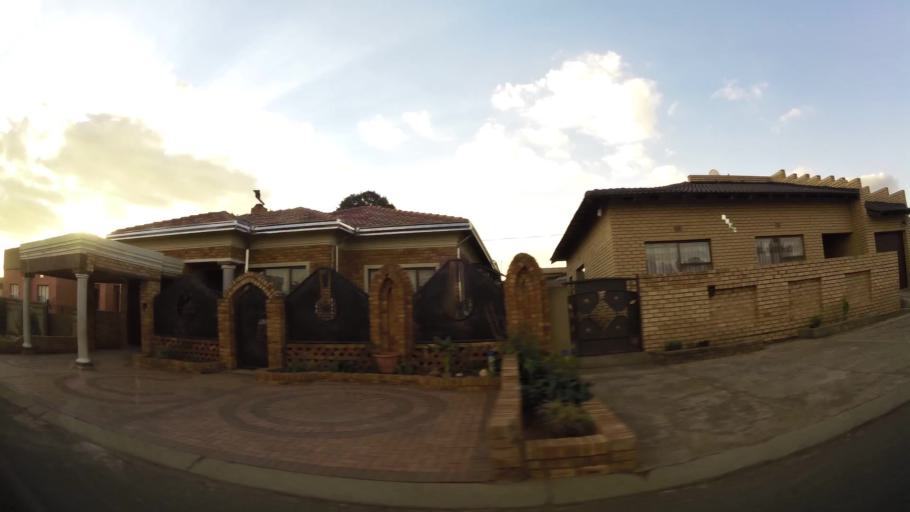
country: ZA
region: Gauteng
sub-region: West Rand District Municipality
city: Krugersdorp
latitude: -26.0822
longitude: 27.7555
